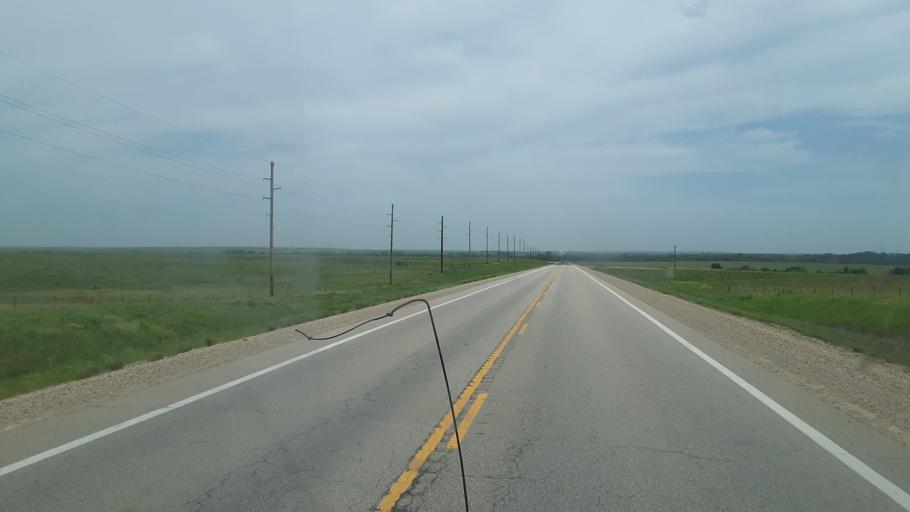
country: US
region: Kansas
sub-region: Greenwood County
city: Eureka
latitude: 37.8380
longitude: -96.1261
